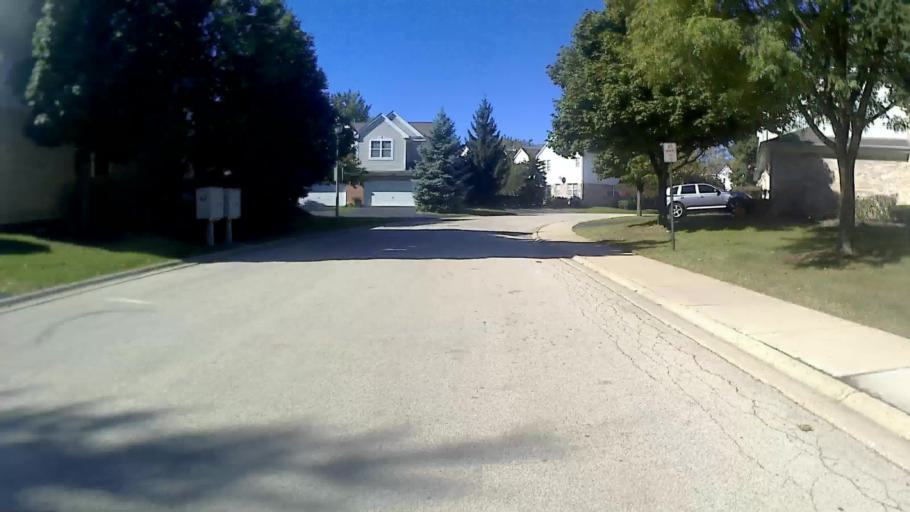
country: US
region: Illinois
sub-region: DuPage County
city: Itasca
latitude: 41.9906
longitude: -88.0168
